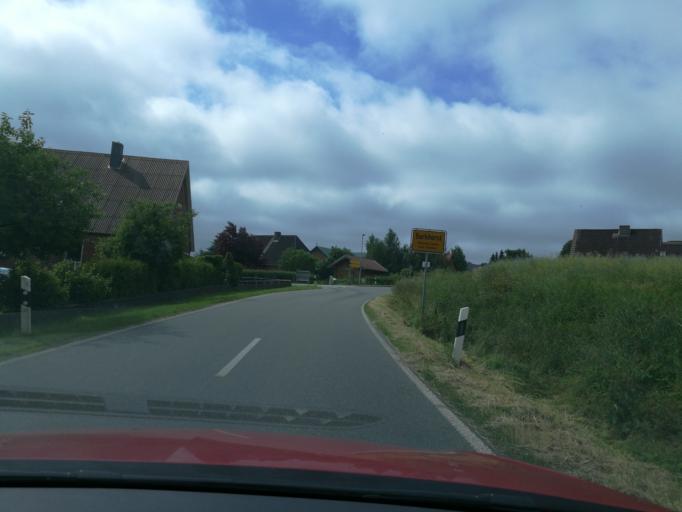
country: DE
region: Schleswig-Holstein
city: Lasbek
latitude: 53.7471
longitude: 10.3791
